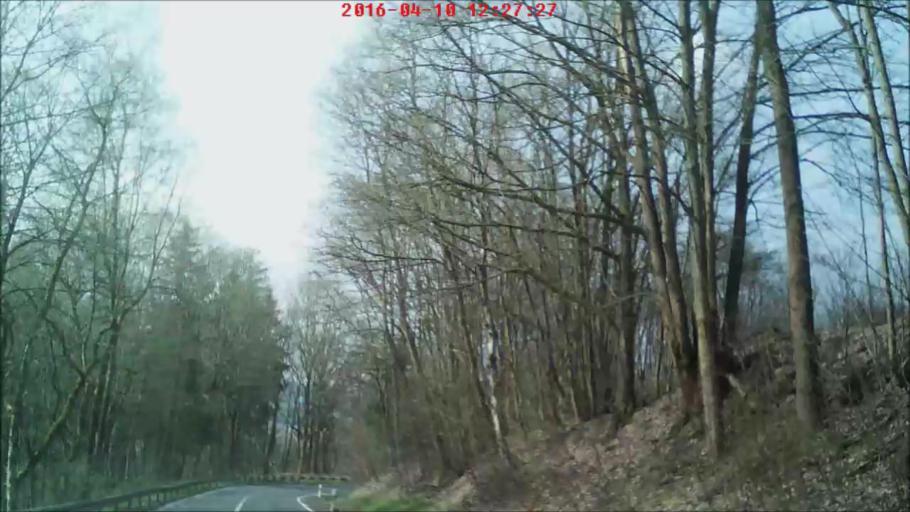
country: DE
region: Thuringia
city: Springstille
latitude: 50.6854
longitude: 10.5445
